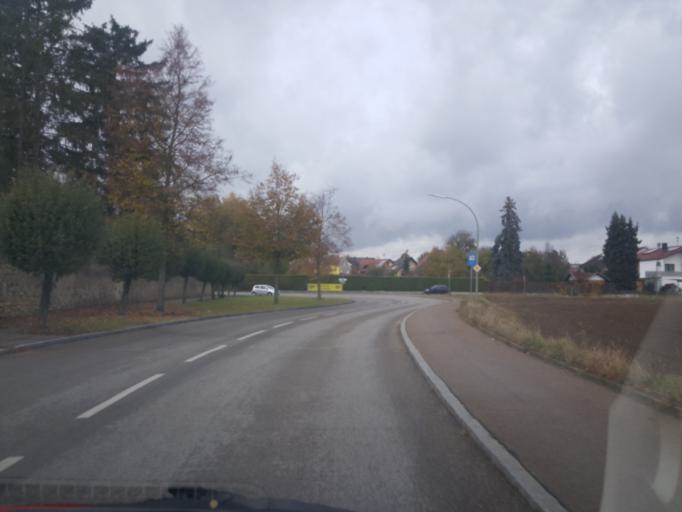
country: DE
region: Bavaria
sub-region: Upper Bavaria
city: Rennertshofen
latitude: 48.7578
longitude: 11.0483
